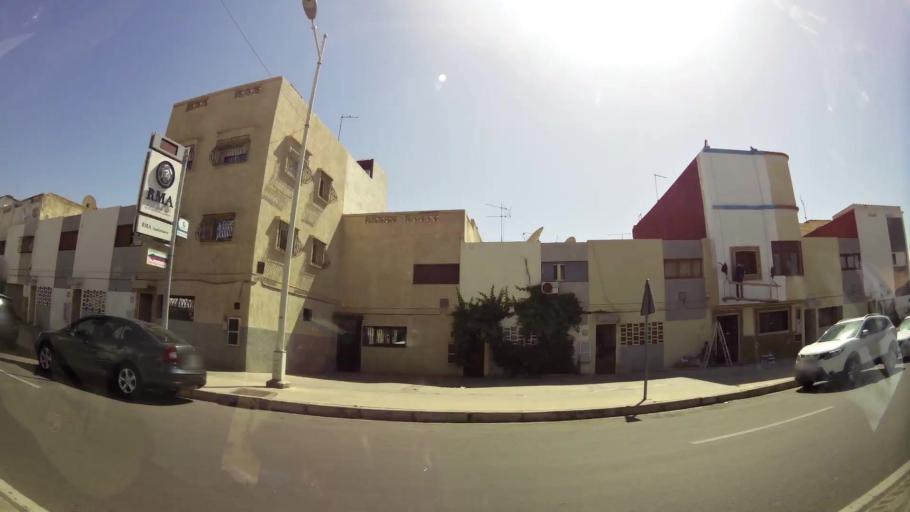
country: MA
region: Souss-Massa-Draa
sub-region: Agadir-Ida-ou-Tnan
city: Agadir
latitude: 30.4240
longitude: -9.5880
